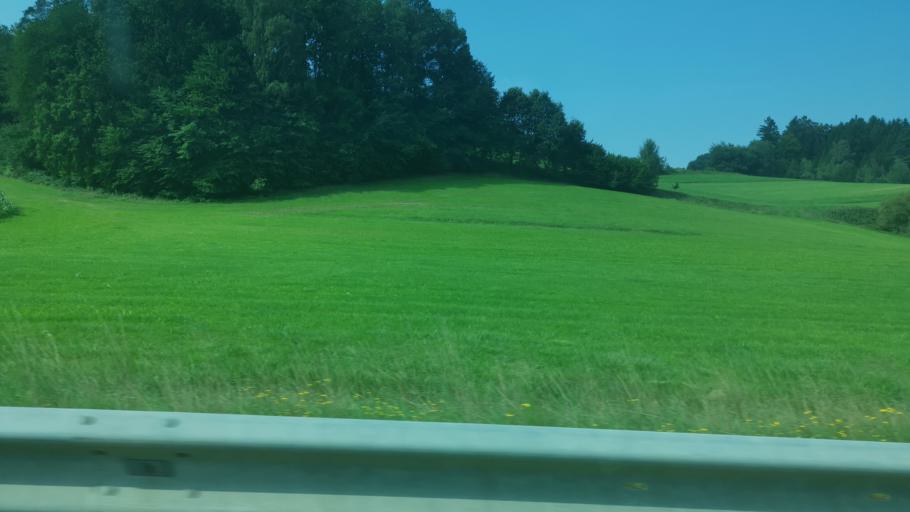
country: DE
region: Bavaria
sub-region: Upper Palatinate
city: Chamerau
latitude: 49.1918
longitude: 12.7307
